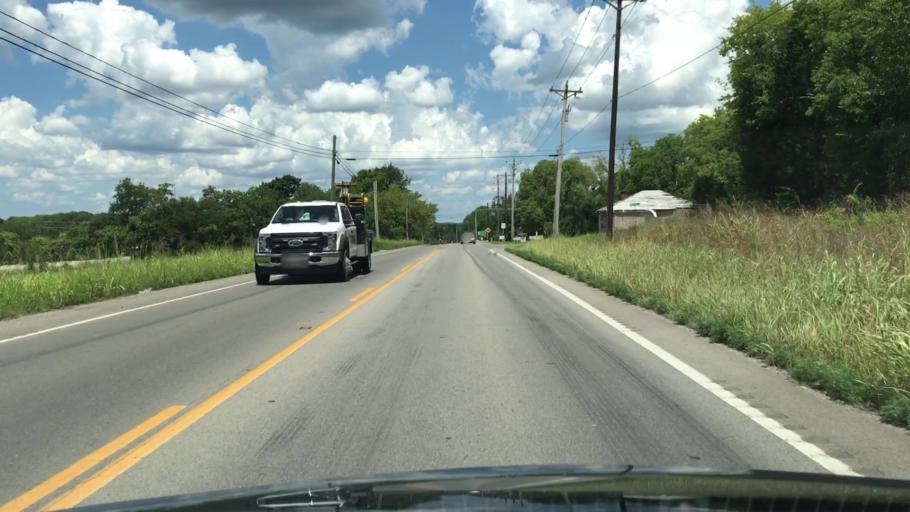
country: US
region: Tennessee
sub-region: Williamson County
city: Nolensville
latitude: 35.9361
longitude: -86.6604
